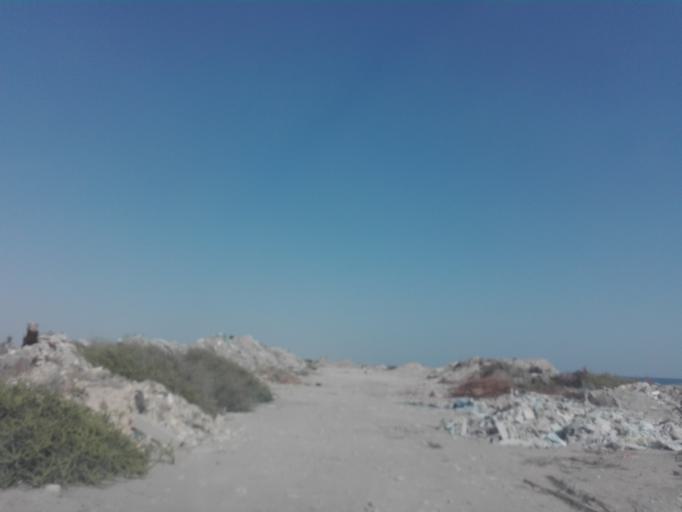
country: TN
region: Qabis
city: Gabes
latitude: 33.9676
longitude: 10.0634
